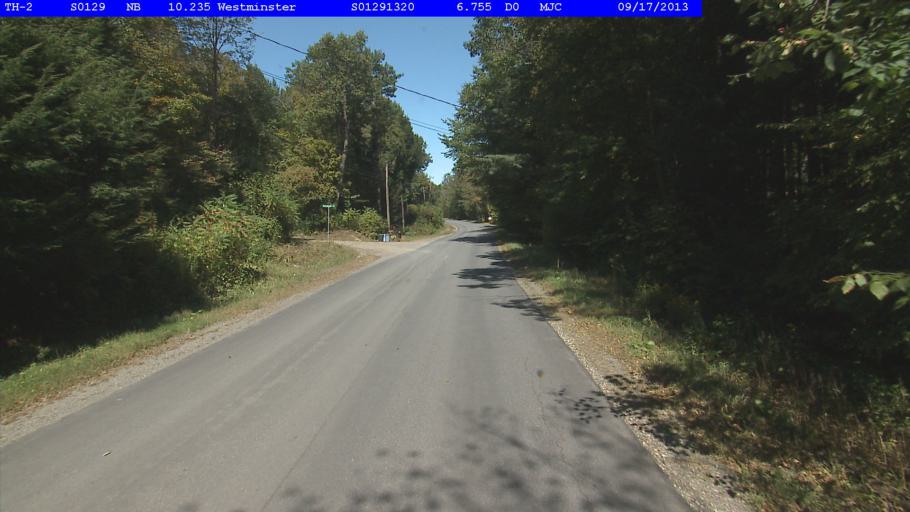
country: US
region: Vermont
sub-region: Windham County
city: Rockingham
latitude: 43.1117
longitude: -72.5372
